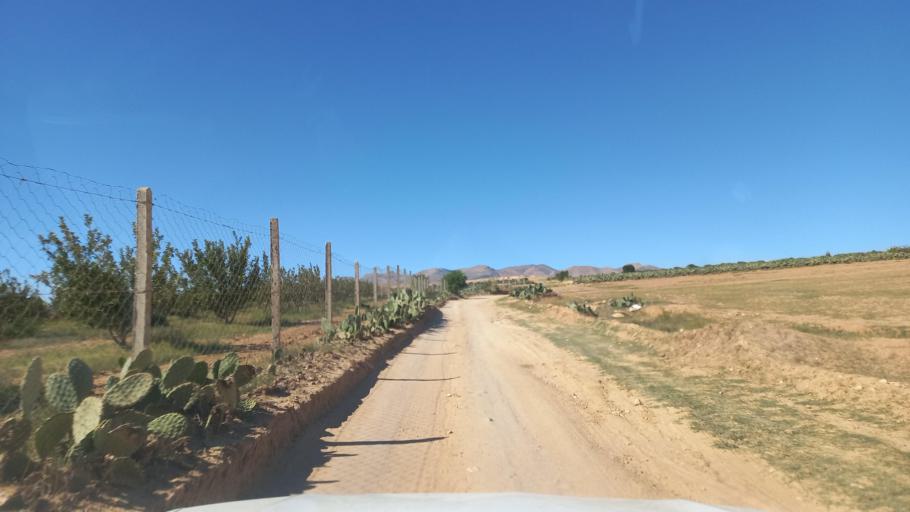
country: TN
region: Al Qasrayn
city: Sbiba
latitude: 35.3723
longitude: 9.0937
